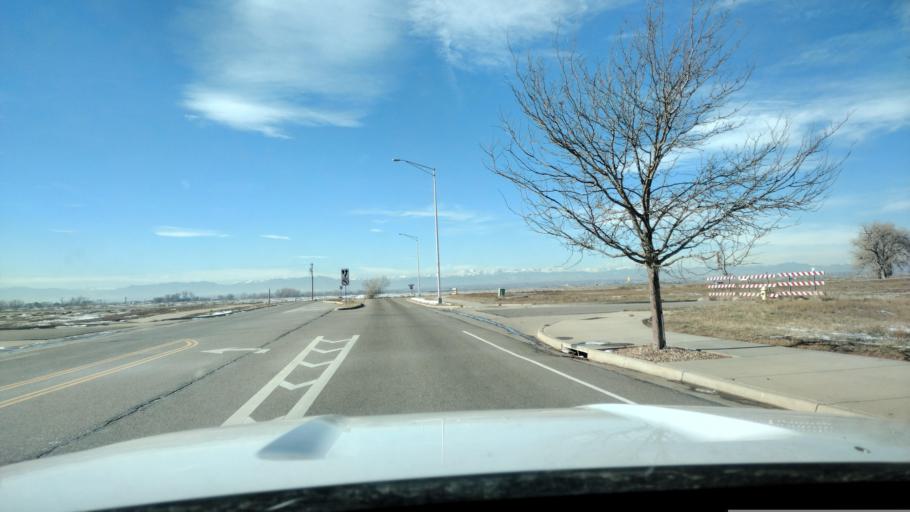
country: US
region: Colorado
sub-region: Adams County
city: Brighton
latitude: 39.9240
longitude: -104.8163
